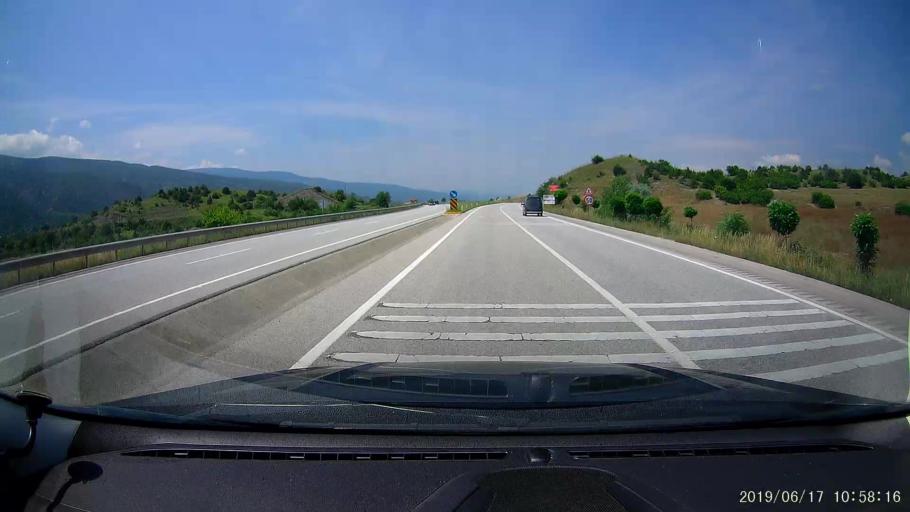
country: TR
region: Kastamonu
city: Tosya
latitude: 41.0449
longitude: 34.2285
